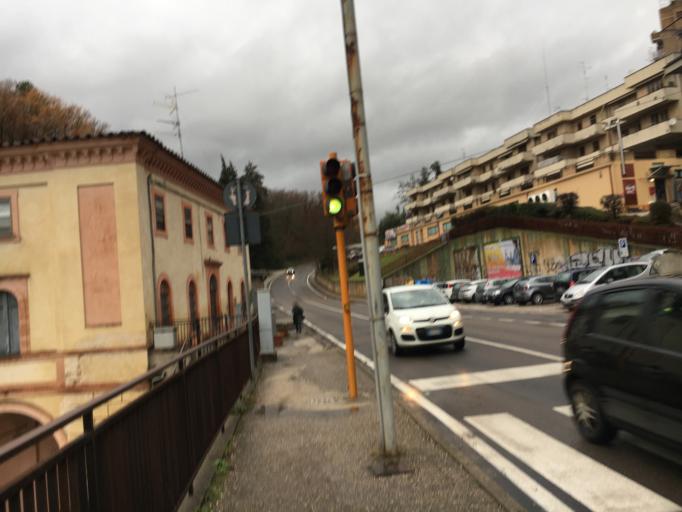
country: IT
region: Umbria
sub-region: Provincia di Perugia
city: Perugia
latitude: 43.1145
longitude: 12.3763
